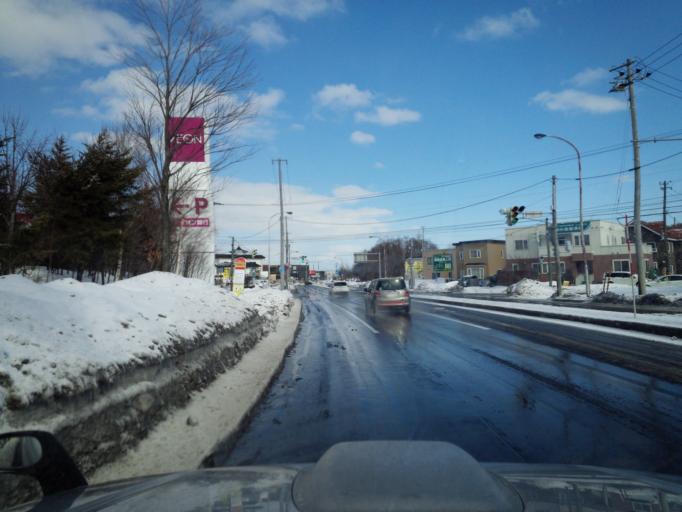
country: JP
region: Hokkaido
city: Kitahiroshima
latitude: 43.0001
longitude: 141.4608
